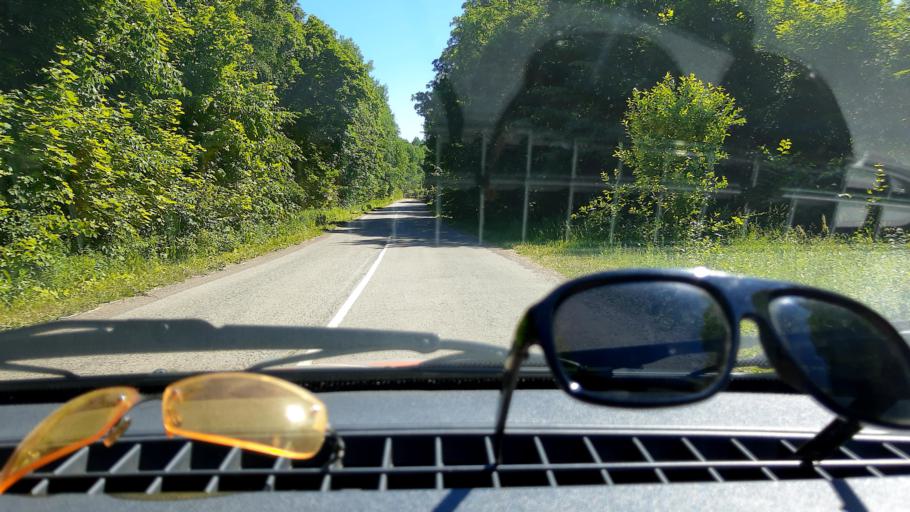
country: RU
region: Bashkortostan
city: Ulu-Telyak
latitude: 54.8082
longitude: 57.0364
